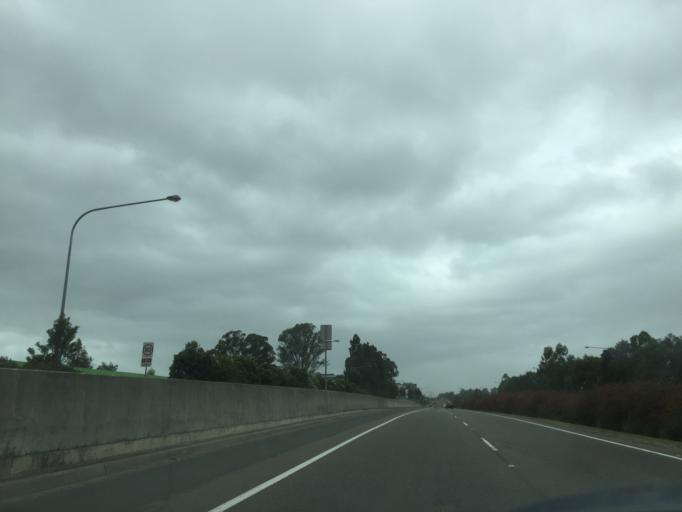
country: AU
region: New South Wales
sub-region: Blacktown
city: Stanhope Gardens
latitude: -33.7284
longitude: 150.9415
